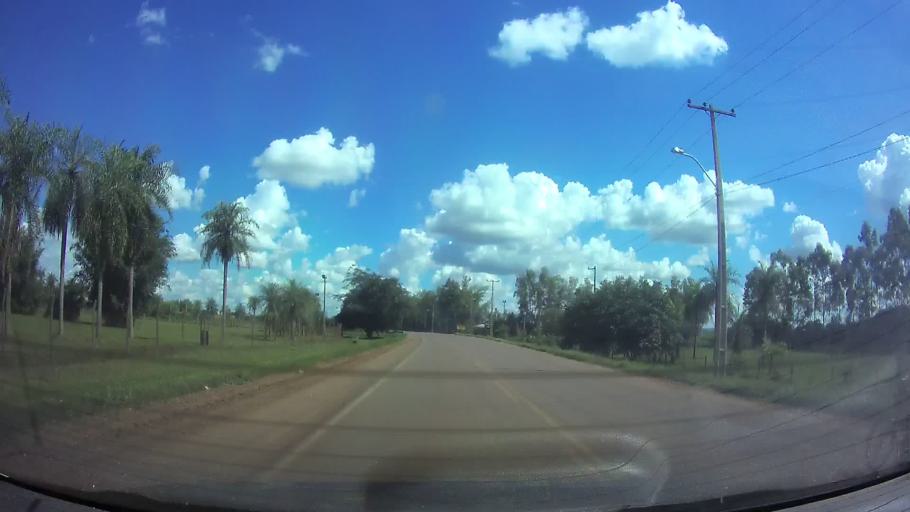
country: PY
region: Guaira
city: Coronel Martinez
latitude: -25.7741
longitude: -56.6522
